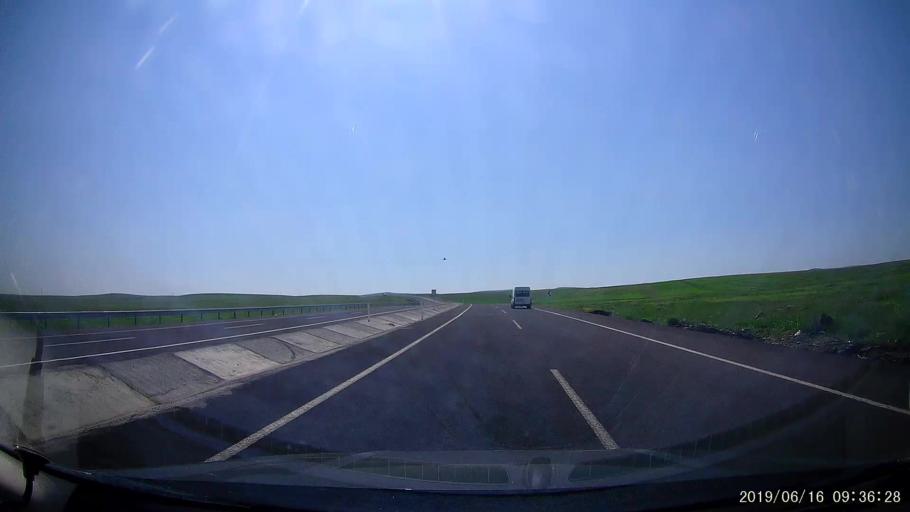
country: TR
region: Kars
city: Kars
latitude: 40.5579
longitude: 43.1729
